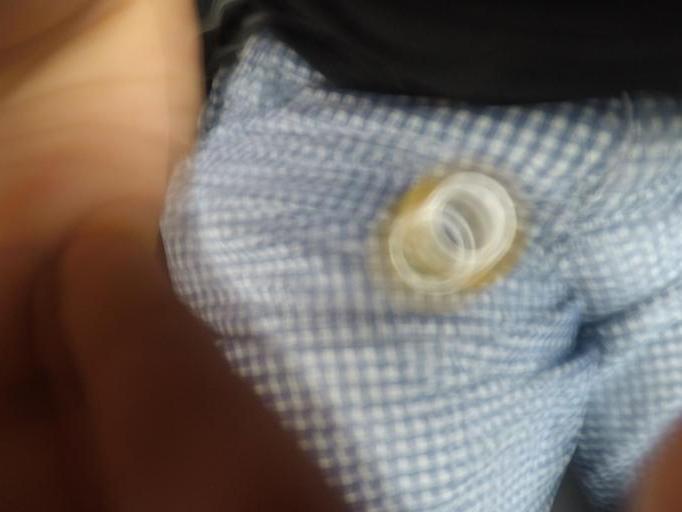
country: MX
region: Oaxaca
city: Matias Romero
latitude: 16.8783
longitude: -95.0389
